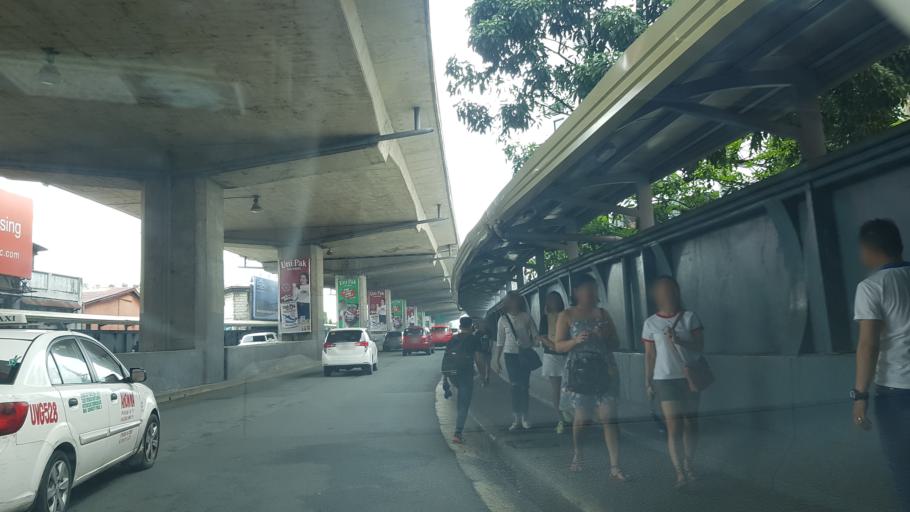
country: PH
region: Metro Manila
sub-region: Makati City
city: Makati City
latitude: 14.5558
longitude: 121.0433
